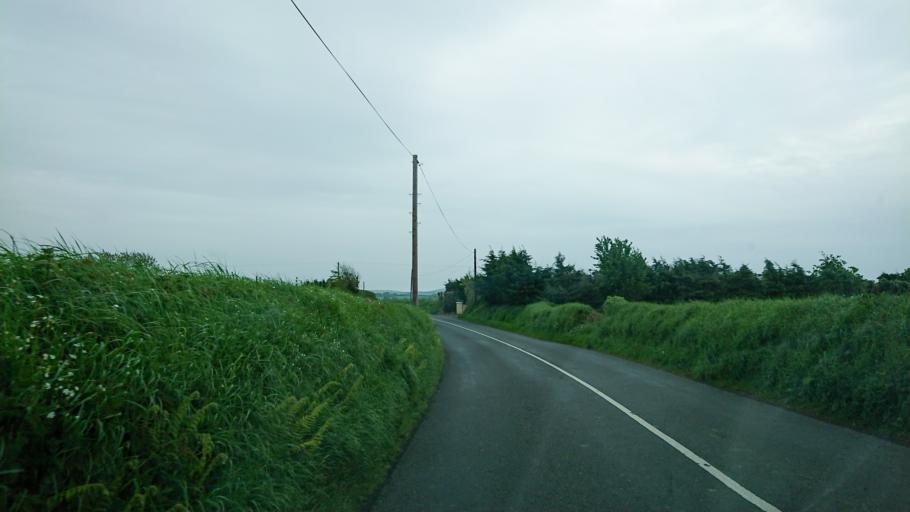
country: IE
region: Munster
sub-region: Waterford
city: Waterford
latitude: 52.2224
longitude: -7.0525
